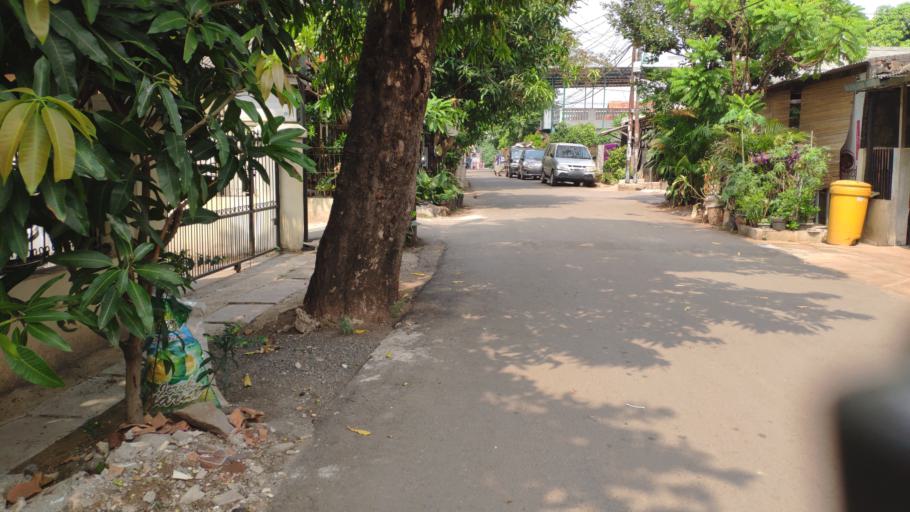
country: ID
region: West Java
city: Pamulang
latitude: -6.3029
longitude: 106.8059
